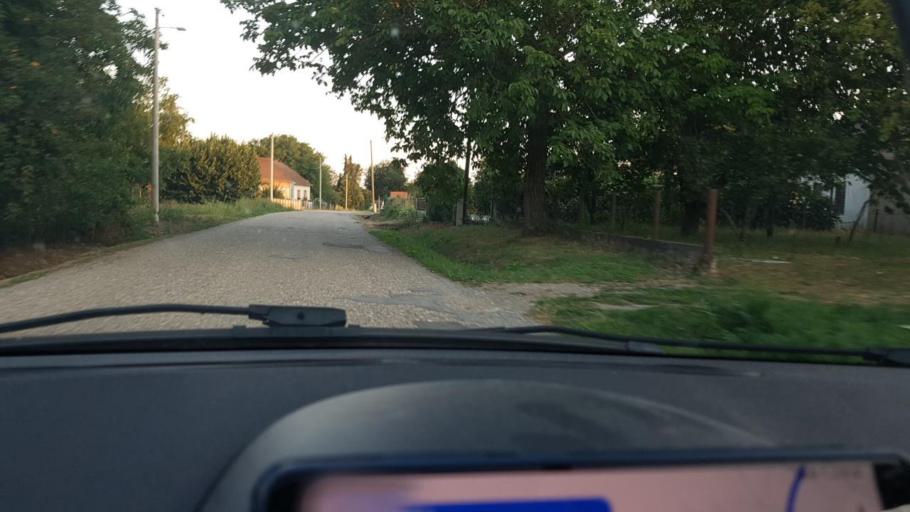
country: HR
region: Bjelovarsko-Bilogorska
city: Zdralovi
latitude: 45.8728
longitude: 17.0011
